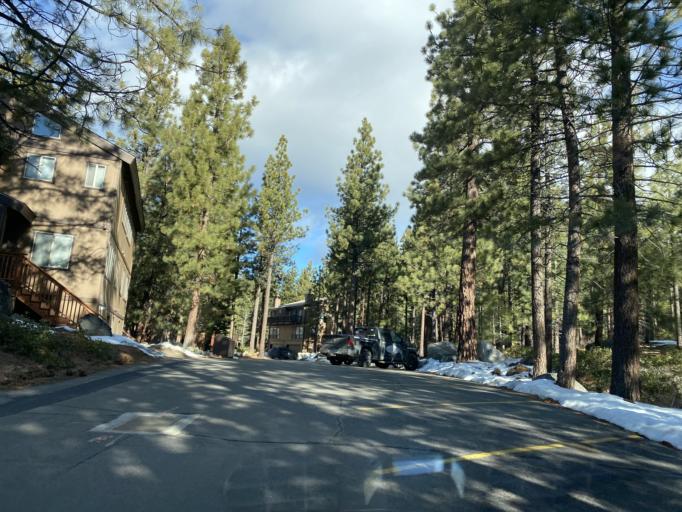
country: US
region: Nevada
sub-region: Douglas County
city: Kingsbury
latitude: 38.9756
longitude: -119.9312
